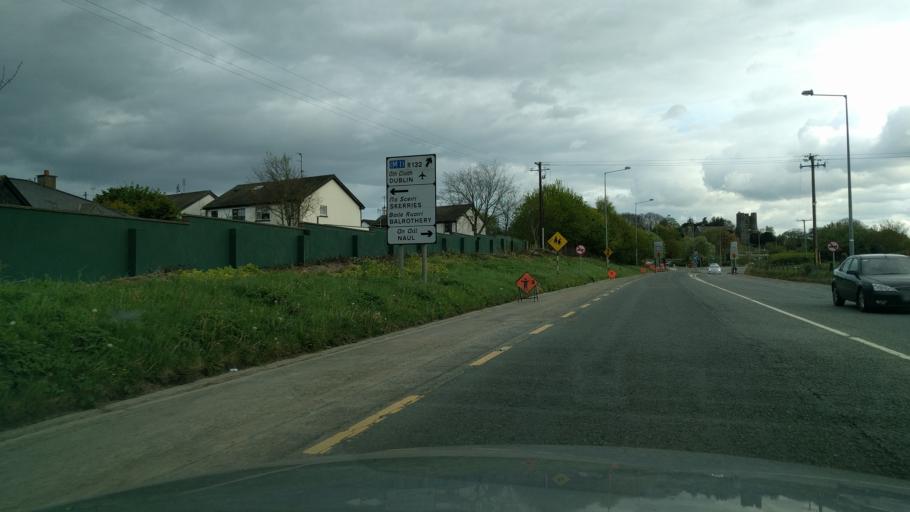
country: IE
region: Leinster
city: Balrothery
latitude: 53.5899
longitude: -6.1884
